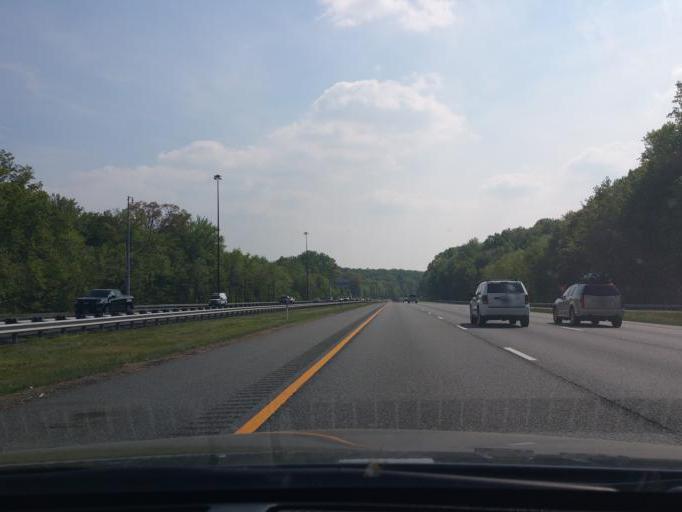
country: US
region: Maryland
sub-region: Harford County
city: Havre de Grace
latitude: 39.5689
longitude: -76.1400
